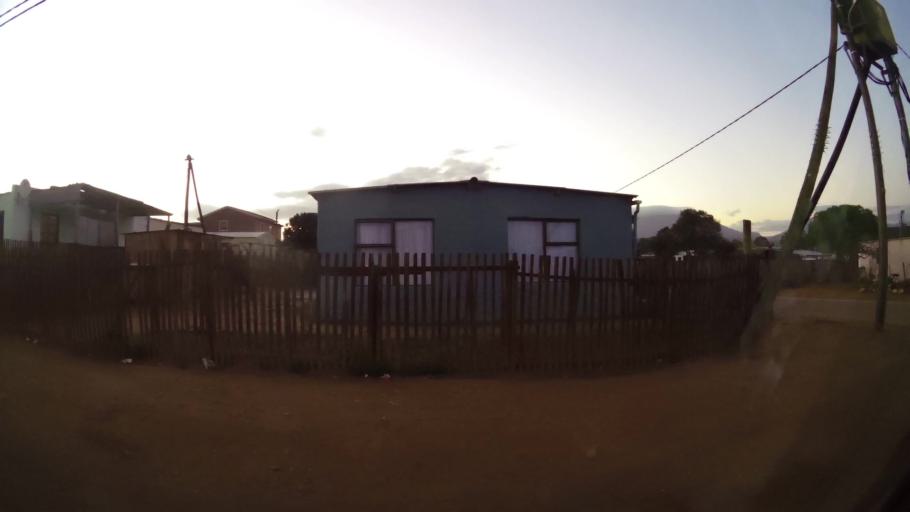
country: ZA
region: Western Cape
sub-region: Eden District Municipality
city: Riversdale
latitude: -34.1006
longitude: 21.2700
